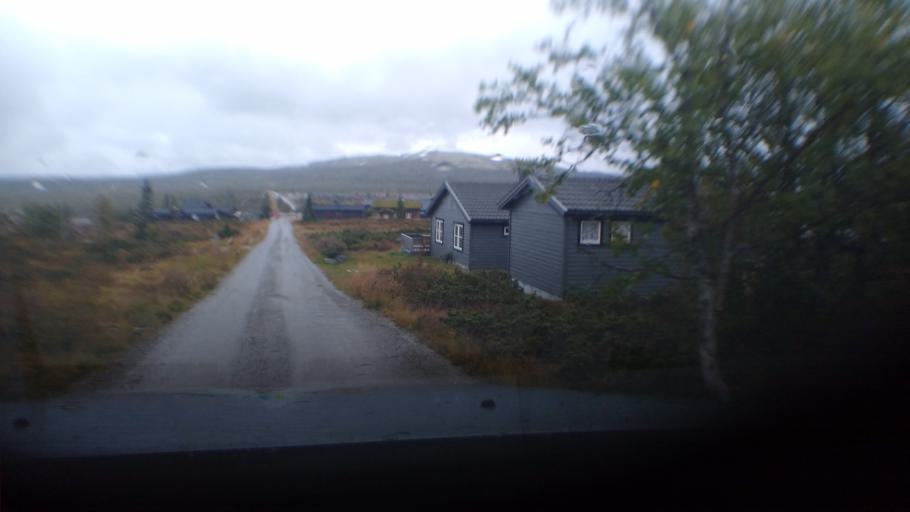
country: NO
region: Oppland
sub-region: Ringebu
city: Ringebu
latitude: 61.6500
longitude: 10.0958
